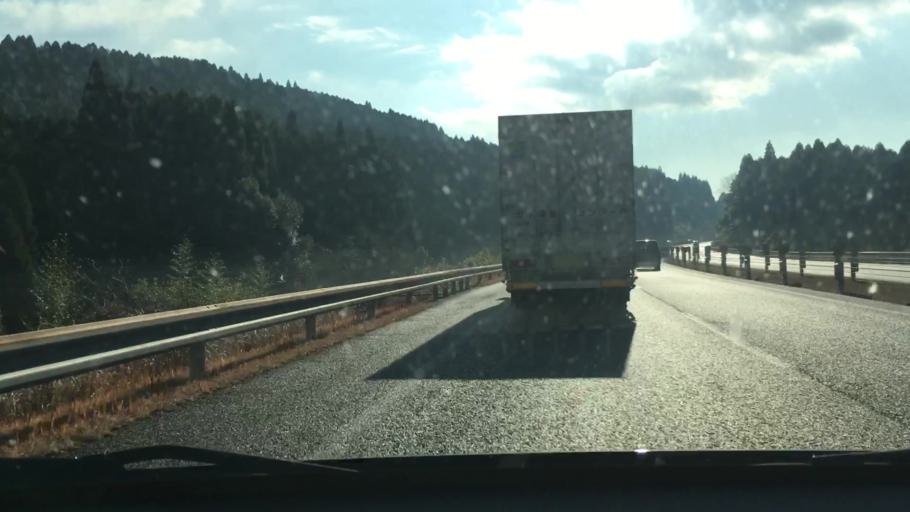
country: JP
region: Kagoshima
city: Okuchi-shinohara
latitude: 31.9609
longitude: 130.7435
